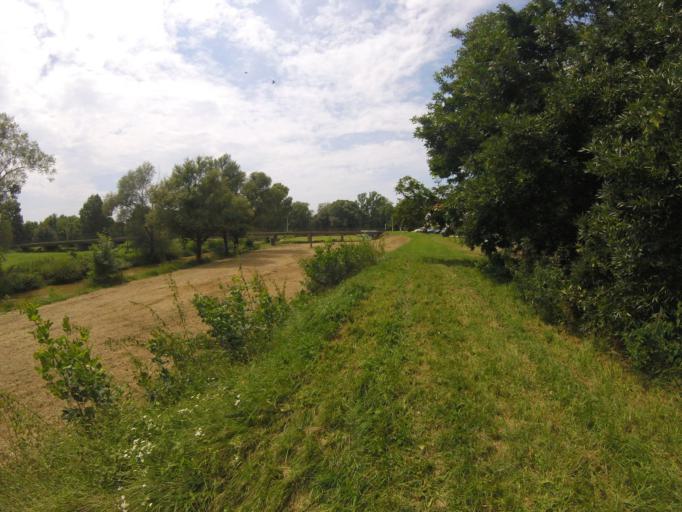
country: HR
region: Medimurska
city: Podturen
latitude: 46.5009
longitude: 16.5763
